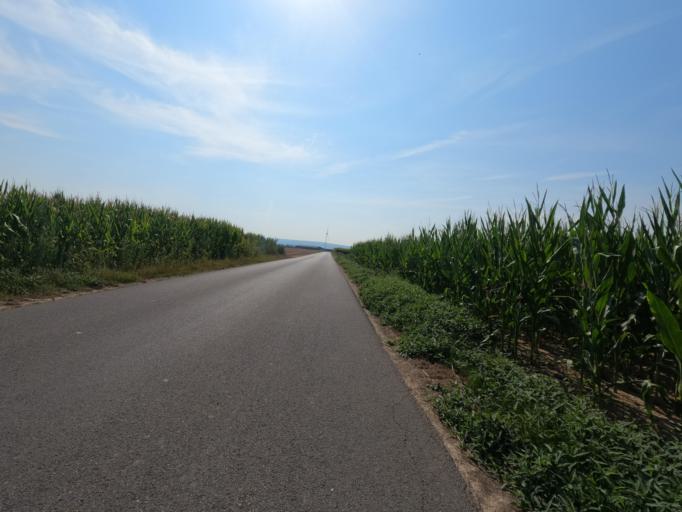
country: DE
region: North Rhine-Westphalia
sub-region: Regierungsbezirk Koln
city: Titz
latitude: 50.9906
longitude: 6.3595
